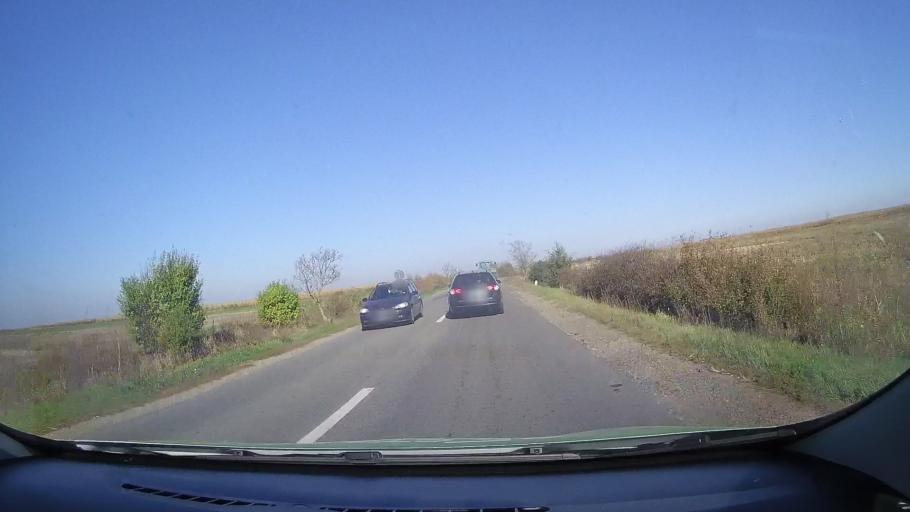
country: RO
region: Satu Mare
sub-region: Comuna Cauas
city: Cauas
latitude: 47.6157
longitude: 22.5364
